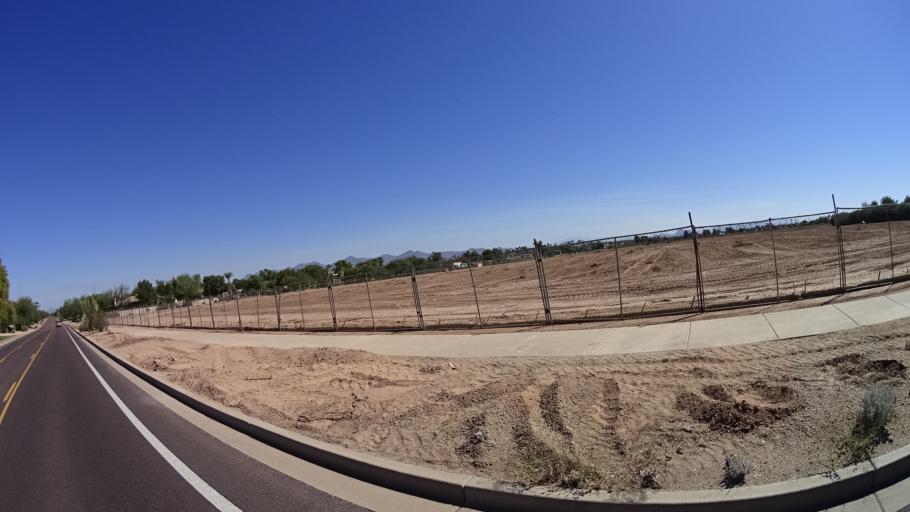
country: US
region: Arizona
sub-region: Maricopa County
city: Paradise Valley
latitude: 33.5374
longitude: -111.9344
